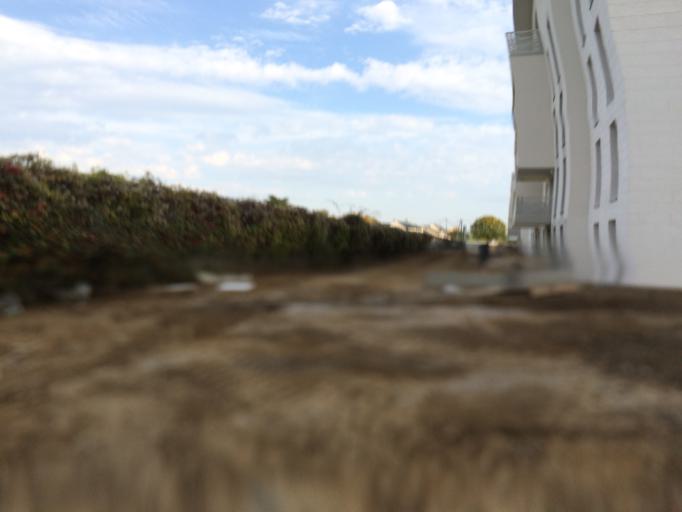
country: FR
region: Ile-de-France
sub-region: Departement de l'Essonne
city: Montlhery
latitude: 48.6453
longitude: 2.2716
